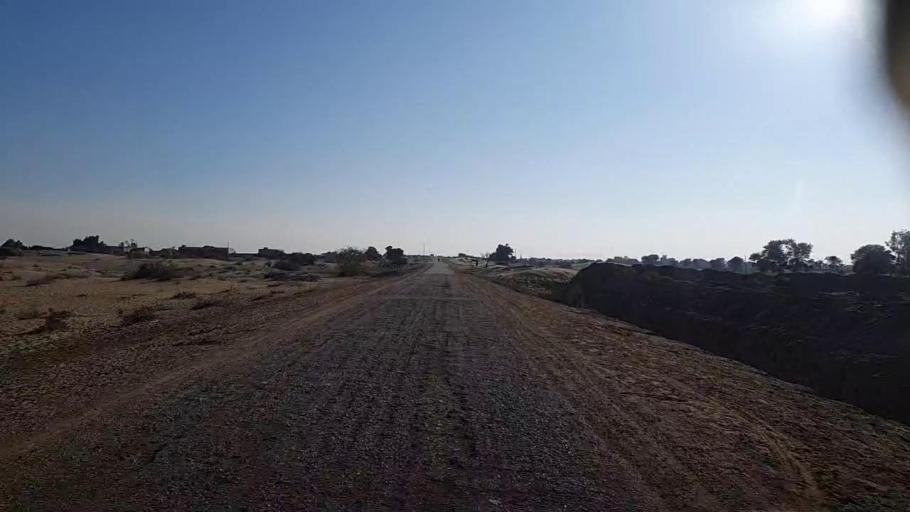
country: PK
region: Sindh
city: Khairpur
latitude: 27.9065
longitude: 69.7501
